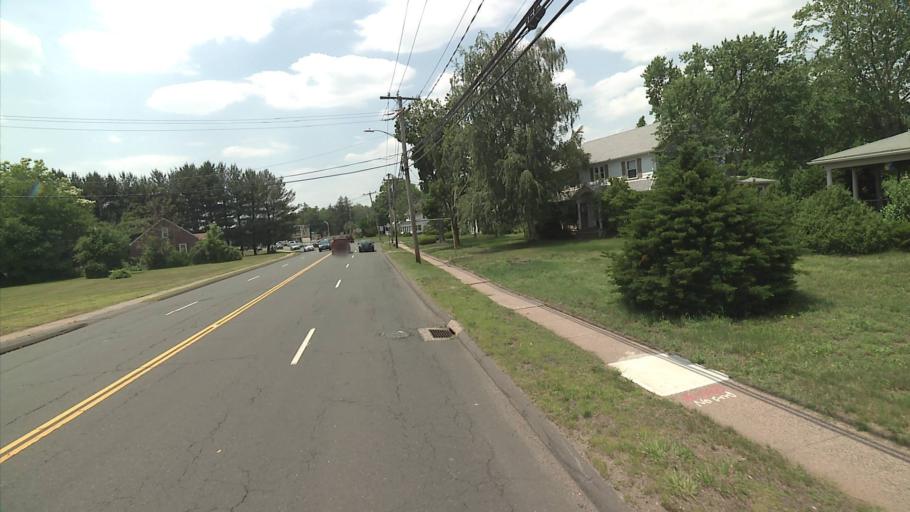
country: US
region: Connecticut
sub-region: Hartford County
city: East Hartford
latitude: 41.7629
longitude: -72.6239
